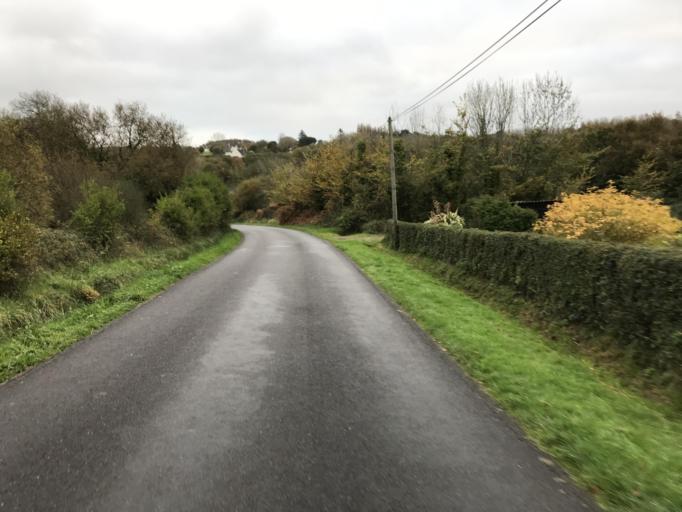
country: FR
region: Brittany
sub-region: Departement du Finistere
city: Logonna-Daoulas
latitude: 48.3331
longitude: -4.2999
